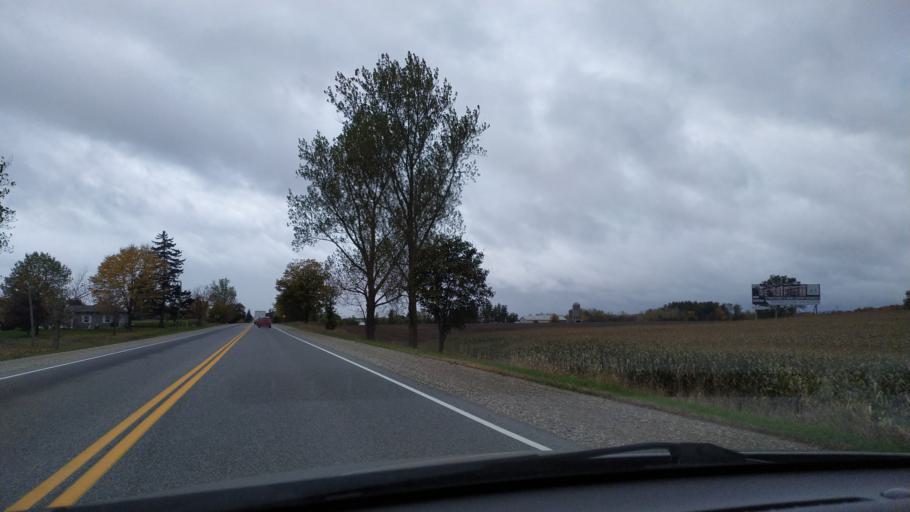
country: CA
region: Ontario
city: Stratford
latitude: 43.3693
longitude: -80.8057
